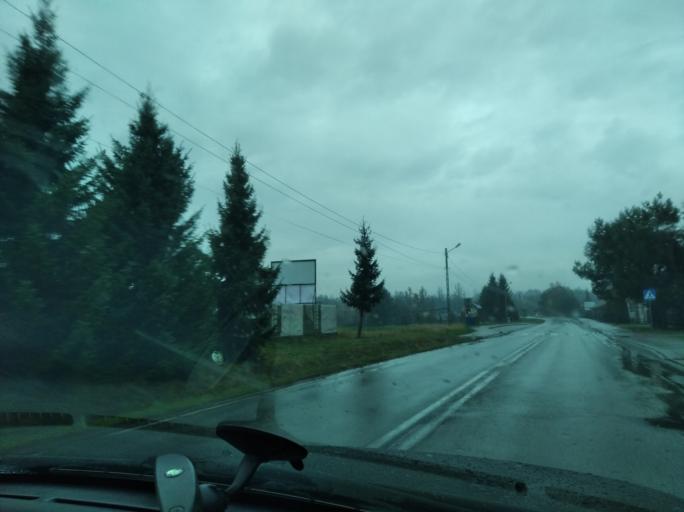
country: PL
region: Subcarpathian Voivodeship
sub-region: Powiat lancucki
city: Albigowa
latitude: 50.0363
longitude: 22.2297
